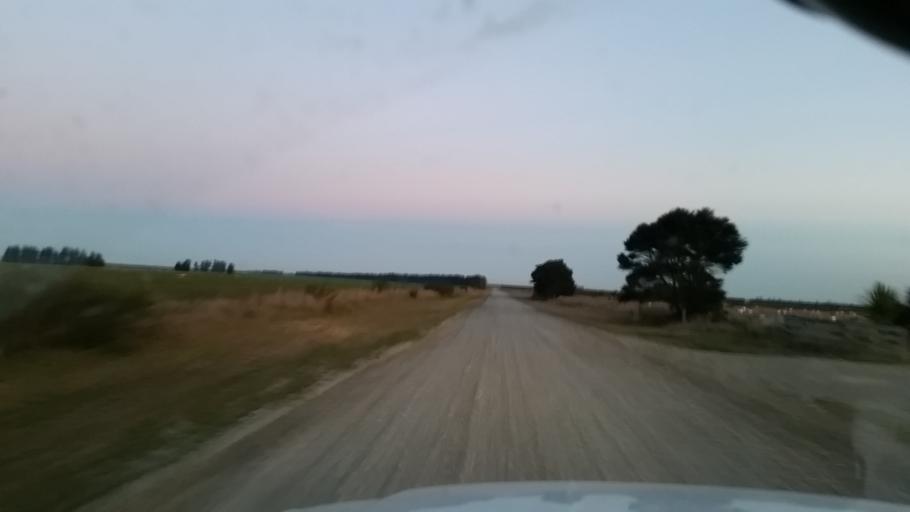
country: NZ
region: Canterbury
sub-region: Ashburton District
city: Tinwald
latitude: -43.9350
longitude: 171.6082
